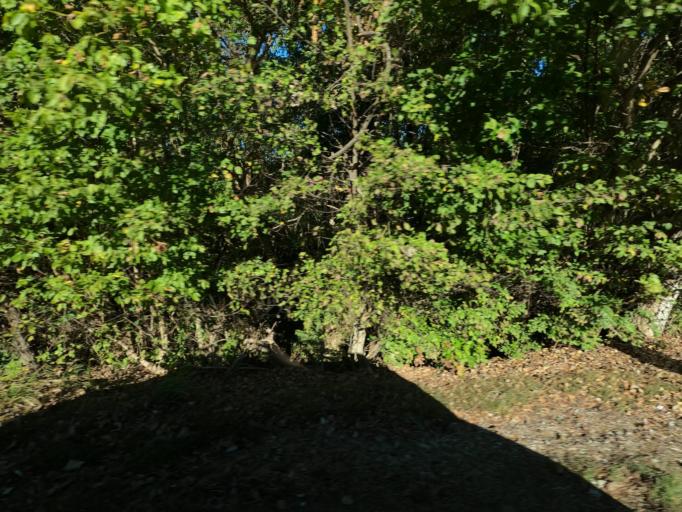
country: US
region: Tennessee
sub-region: Tipton County
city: Brighton
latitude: 35.5129
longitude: -89.7074
